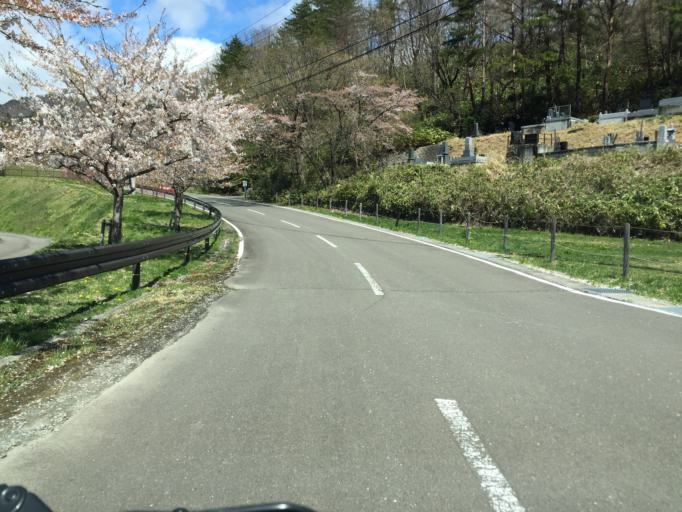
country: JP
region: Fukushima
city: Fukushima-shi
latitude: 37.8395
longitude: 140.4349
